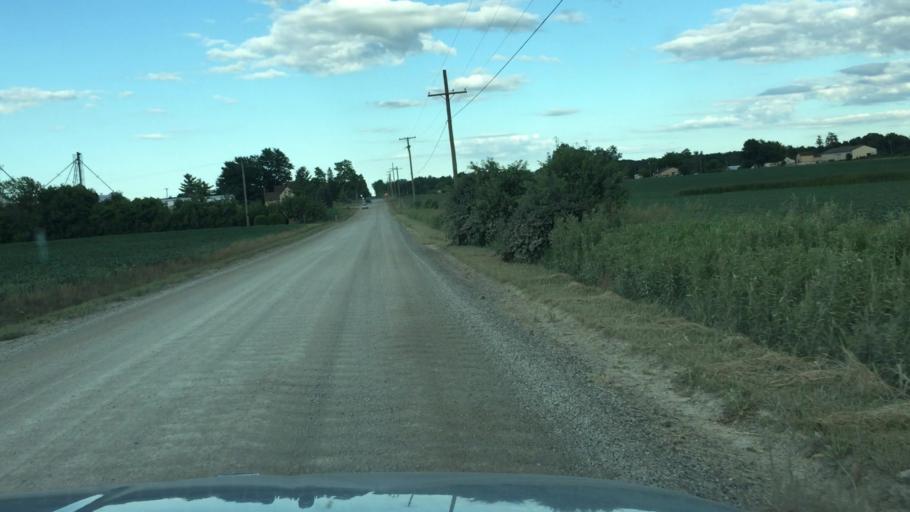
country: US
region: Michigan
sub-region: Saint Clair County
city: Yale
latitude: 43.1442
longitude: -82.8059
